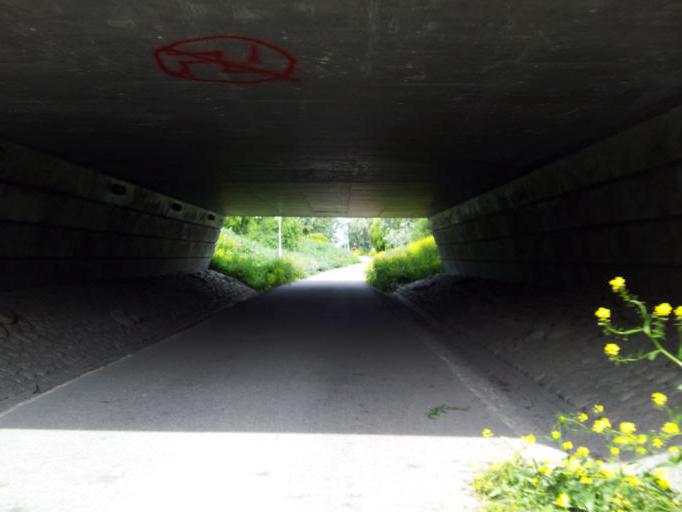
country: SE
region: Uppsala
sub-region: Uppsala Kommun
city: Gamla Uppsala
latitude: 59.8756
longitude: 17.6065
